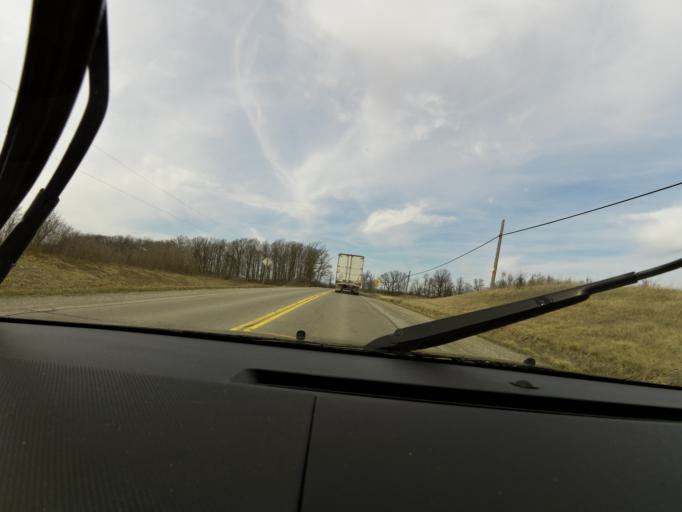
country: CA
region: Ontario
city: Ancaster
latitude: 42.9716
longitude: -79.8694
